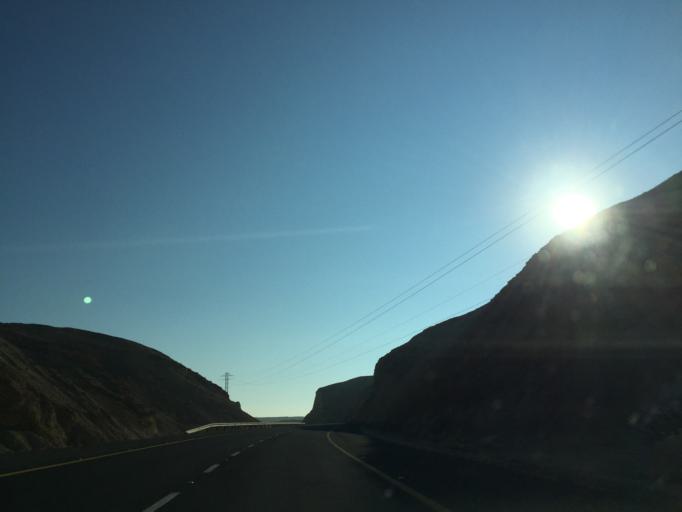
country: IL
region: Southern District
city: Mitzpe Ramon
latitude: 30.2788
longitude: 35.0046
